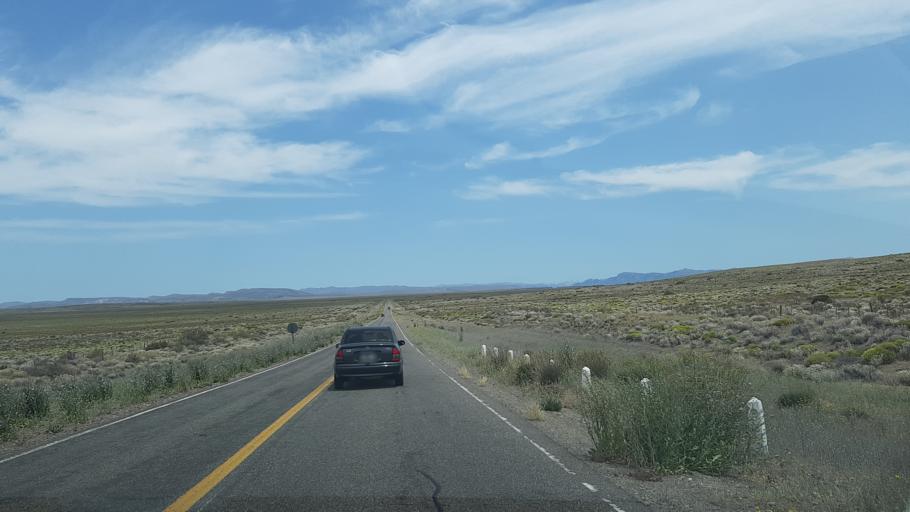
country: AR
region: Rio Negro
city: Pilcaniyeu
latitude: -40.5160
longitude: -70.6904
